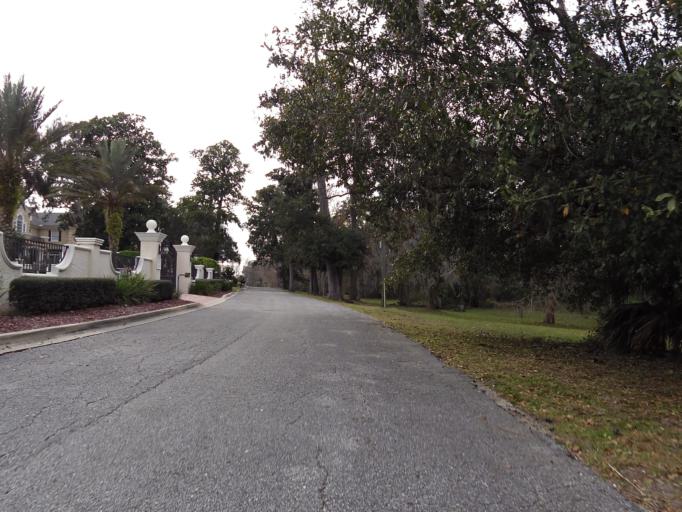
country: US
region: Florida
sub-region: Duval County
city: Jacksonville
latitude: 30.2456
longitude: -81.6334
